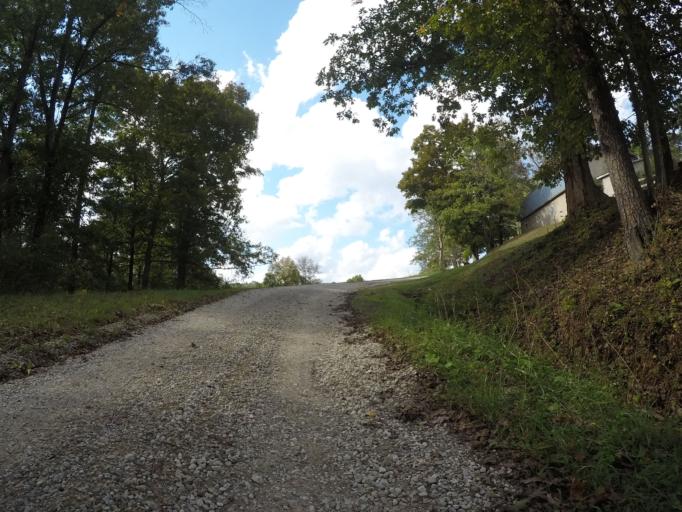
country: US
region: West Virginia
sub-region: Wayne County
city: Lavalette
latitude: 38.3570
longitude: -82.4550
